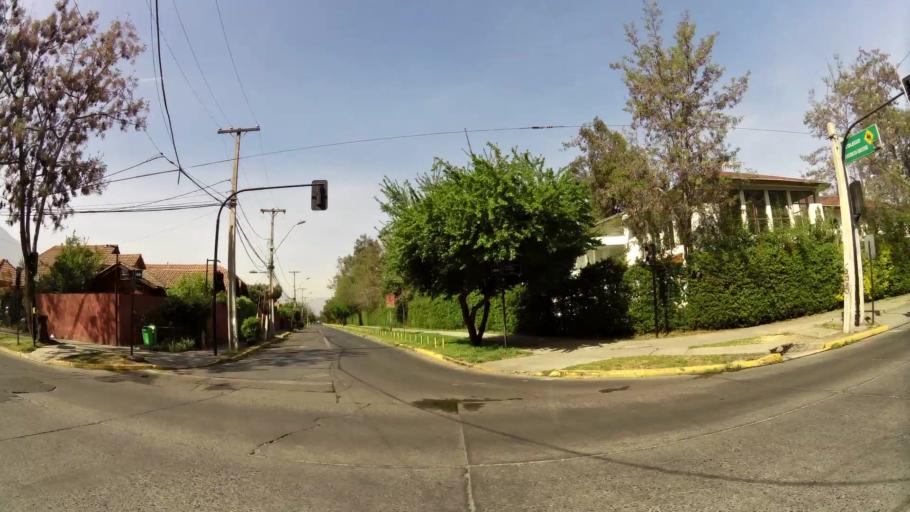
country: CL
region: Santiago Metropolitan
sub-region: Provincia de Santiago
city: Villa Presidente Frei, Nunoa, Santiago, Chile
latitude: -33.5224
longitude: -70.5678
